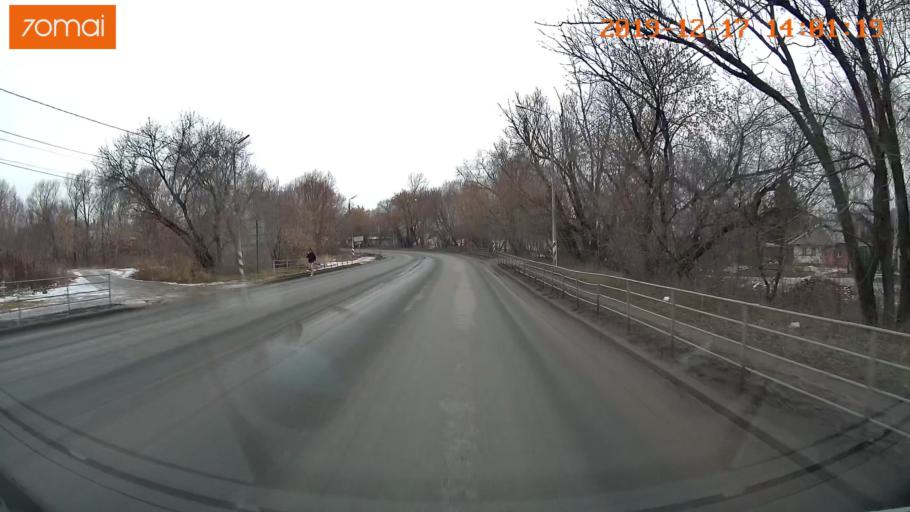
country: RU
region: Rjazan
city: Ryazan'
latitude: 54.6192
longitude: 39.6599
